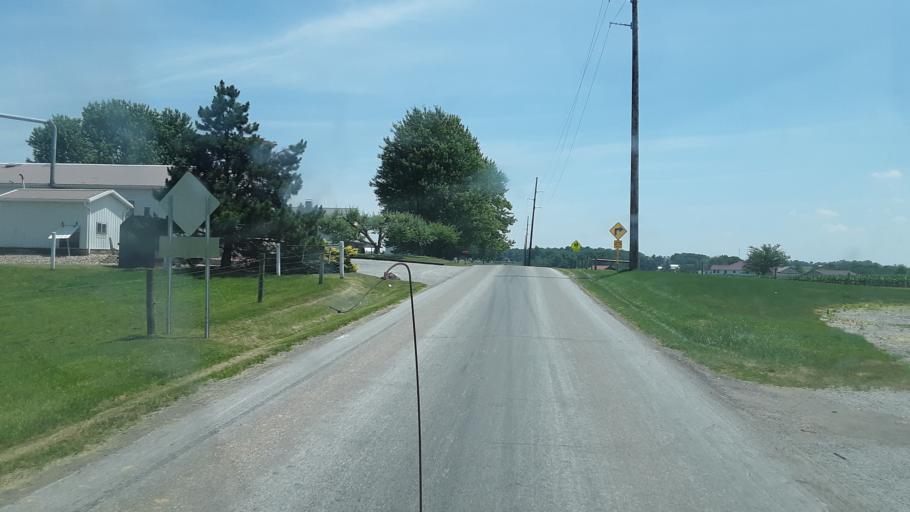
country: US
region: Ohio
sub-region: Wayne County
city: Apple Creek
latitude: 40.7118
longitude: -81.7742
